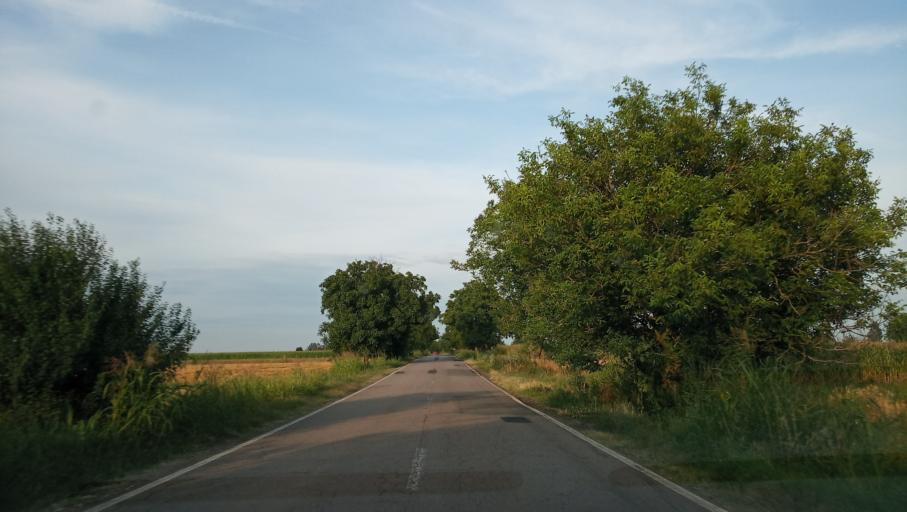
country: RO
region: Giurgiu
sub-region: Comuna Greaca
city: Greaca
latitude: 44.1054
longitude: 26.3068
